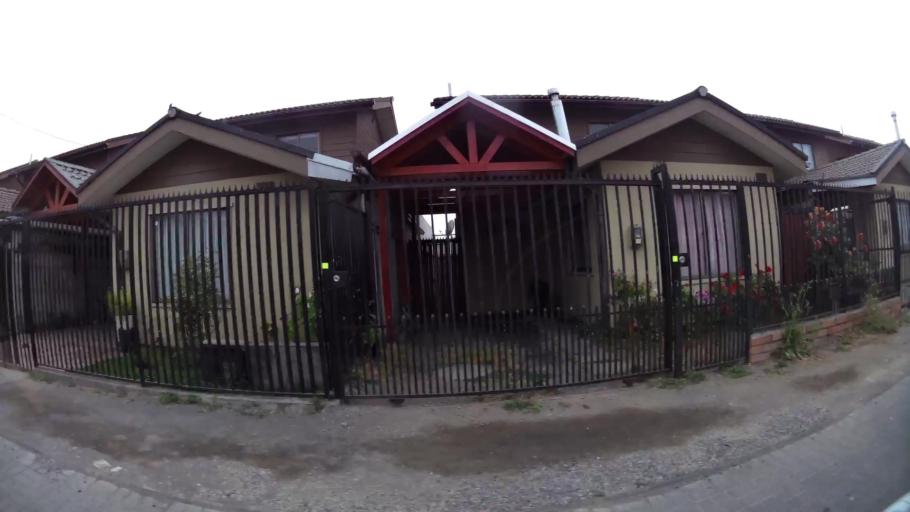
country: CL
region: Biobio
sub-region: Provincia de Concepcion
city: Concepcion
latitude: -36.7861
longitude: -73.0796
